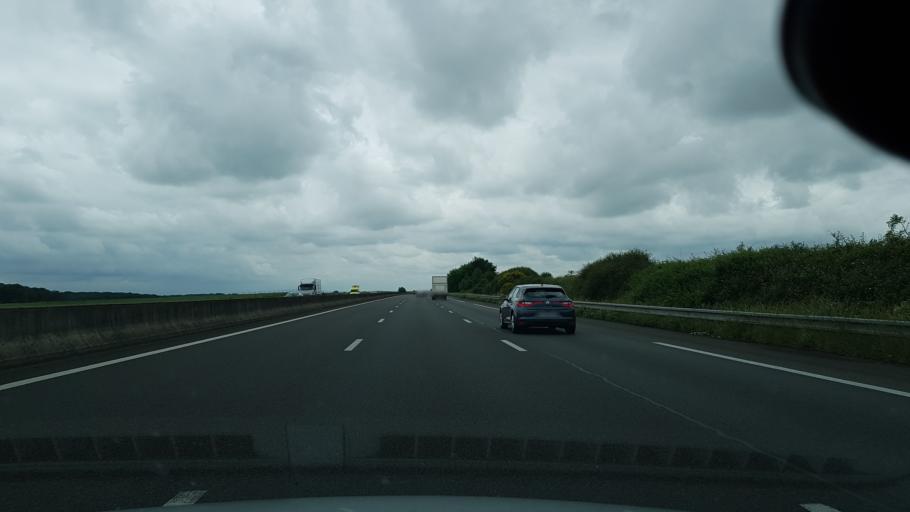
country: FR
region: Centre
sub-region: Departement du Loir-et-Cher
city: Herbault
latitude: 47.5685
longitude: 1.0464
